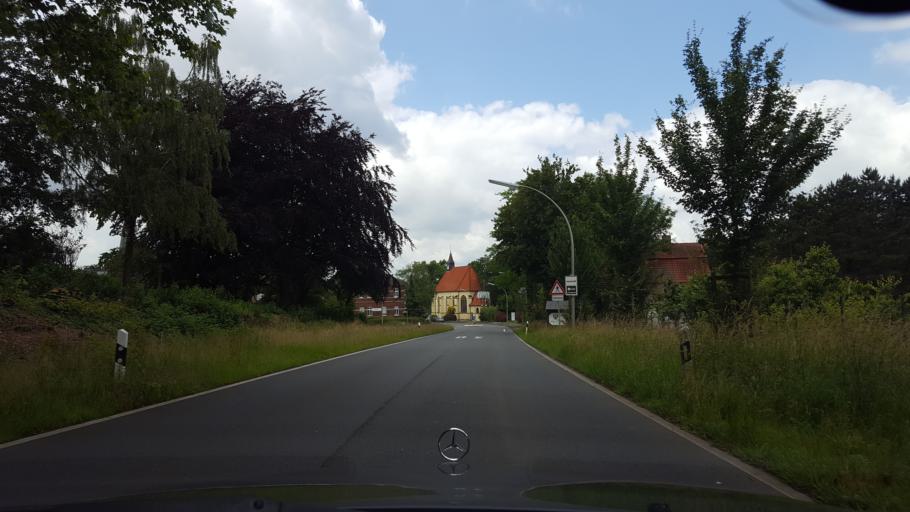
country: DE
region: North Rhine-Westphalia
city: Oer-Erkenschwick
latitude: 51.6299
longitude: 7.2978
